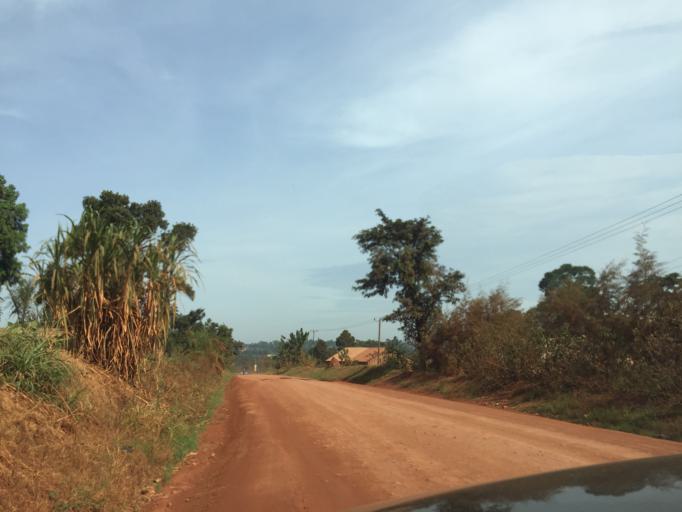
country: UG
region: Central Region
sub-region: Wakiso District
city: Kireka
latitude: 0.4481
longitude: 32.5789
